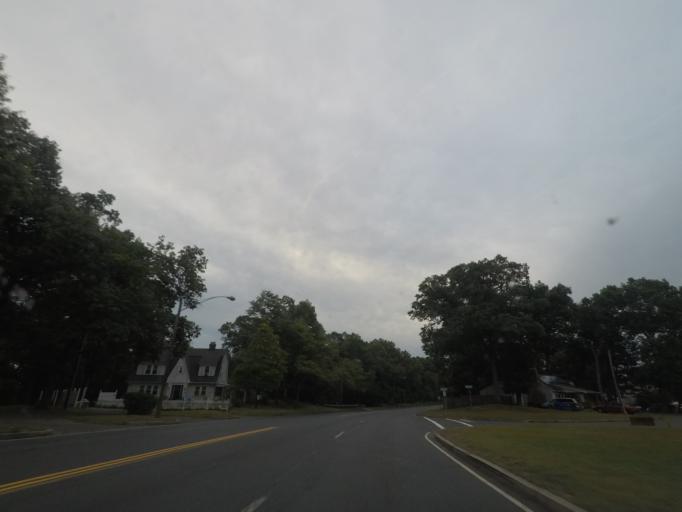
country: US
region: Massachusetts
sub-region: Hampden County
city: Ludlow
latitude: 42.1520
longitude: -72.5309
